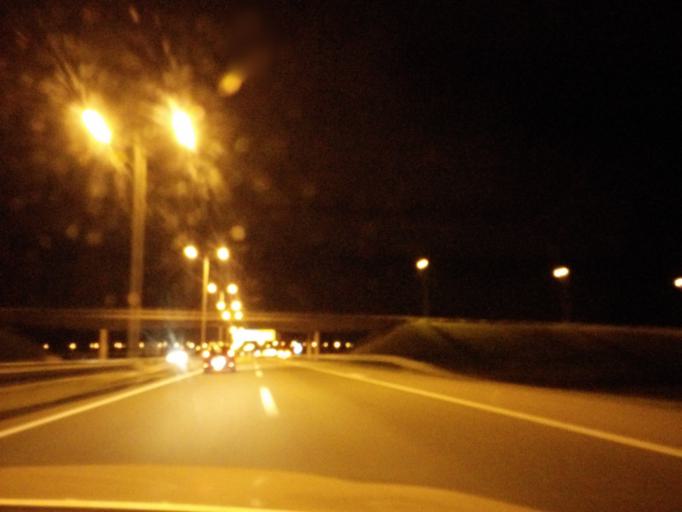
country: RS
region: Autonomna Pokrajina Vojvodina
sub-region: Sremski Okrug
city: Pecinci
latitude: 44.9204
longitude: 19.9604
